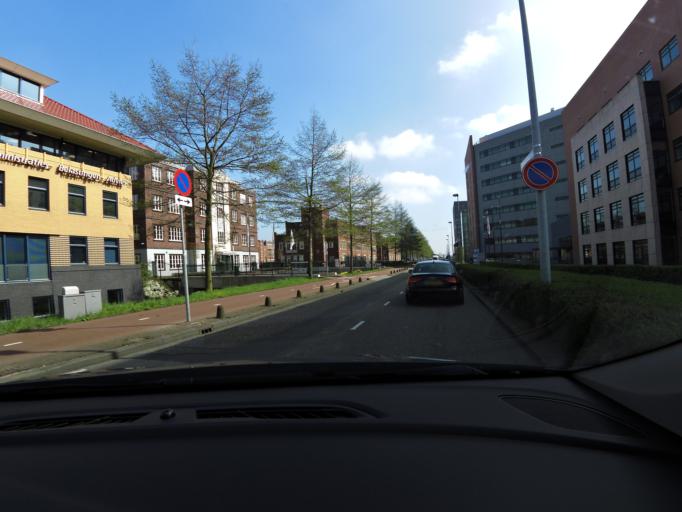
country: NL
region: South Holland
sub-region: Gemeente Den Haag
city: Ypenburg
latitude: 52.0506
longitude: 4.3482
